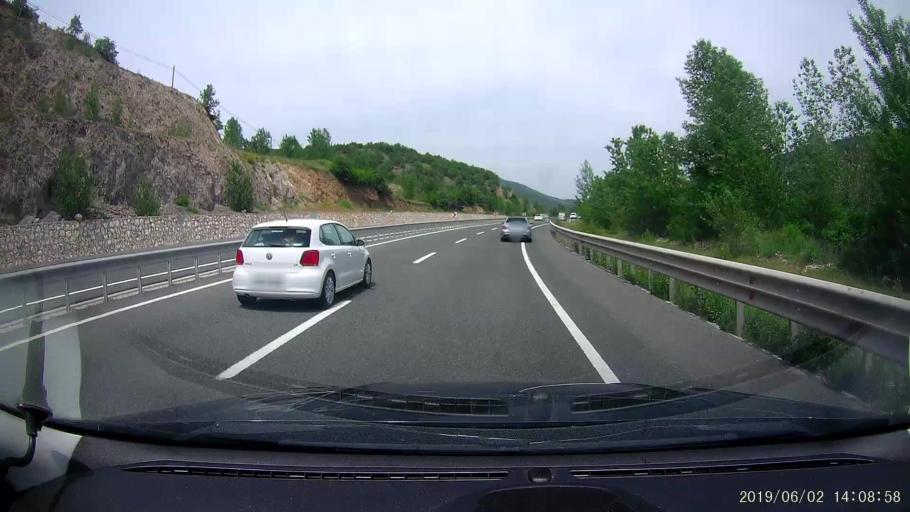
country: TR
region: Cankiri
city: Ilgaz
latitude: 40.8896
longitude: 33.7351
